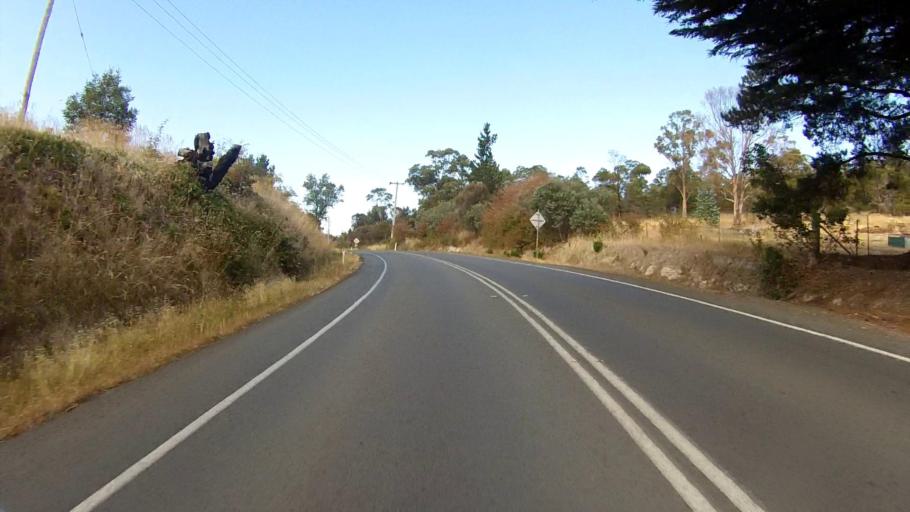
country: AU
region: Tasmania
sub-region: Brighton
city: Bridgewater
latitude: -42.7301
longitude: 147.1780
